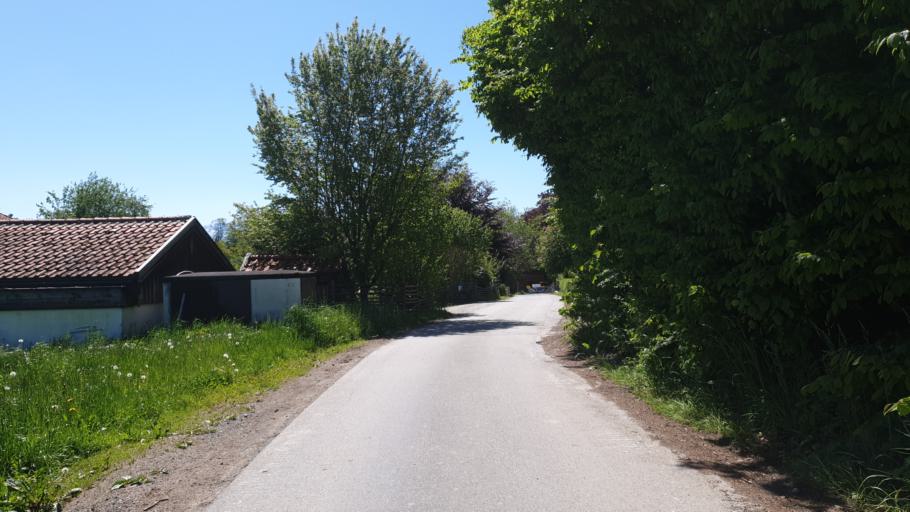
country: DE
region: Bavaria
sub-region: Upper Bavaria
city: Iffeldorf
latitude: 47.7678
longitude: 11.2995
